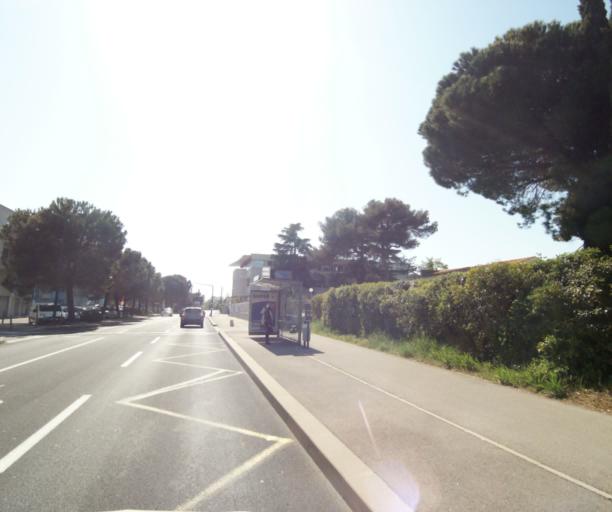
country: FR
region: Languedoc-Roussillon
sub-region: Departement de l'Herault
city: Castelnau-le-Lez
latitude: 43.6139
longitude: 3.9060
